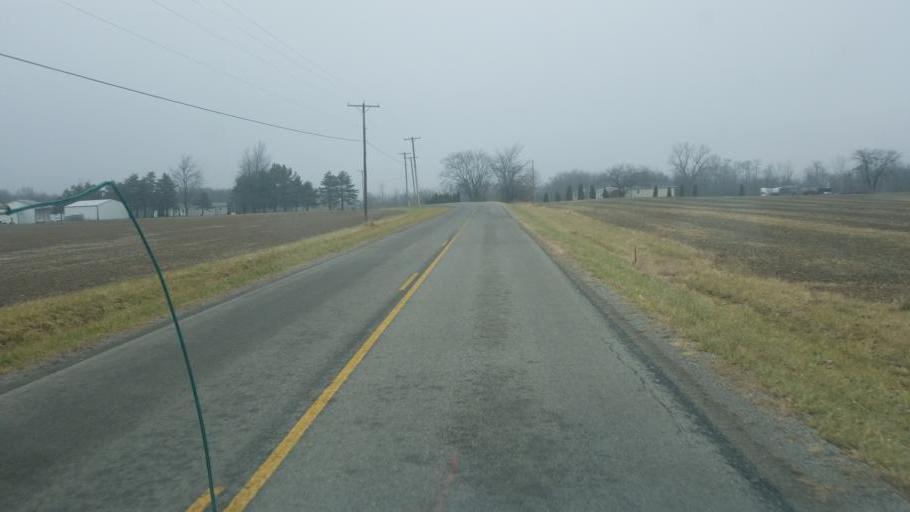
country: US
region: Ohio
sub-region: Champaign County
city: North Lewisburg
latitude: 40.3488
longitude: -83.5557
